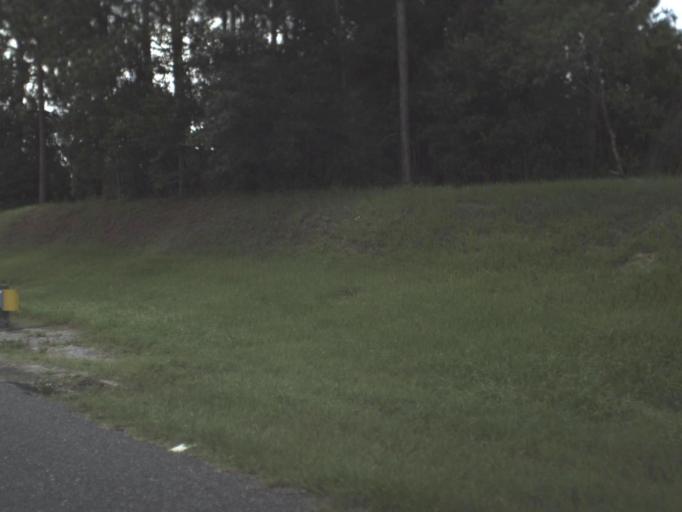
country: US
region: Florida
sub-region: Hernando County
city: Hill 'n Dale
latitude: 28.5231
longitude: -82.2573
